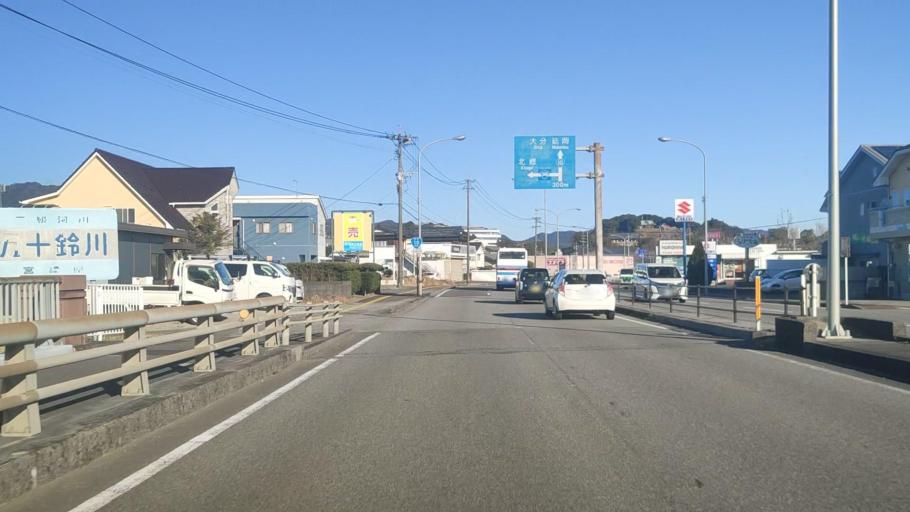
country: JP
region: Miyazaki
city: Nobeoka
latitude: 32.4652
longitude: 131.6483
